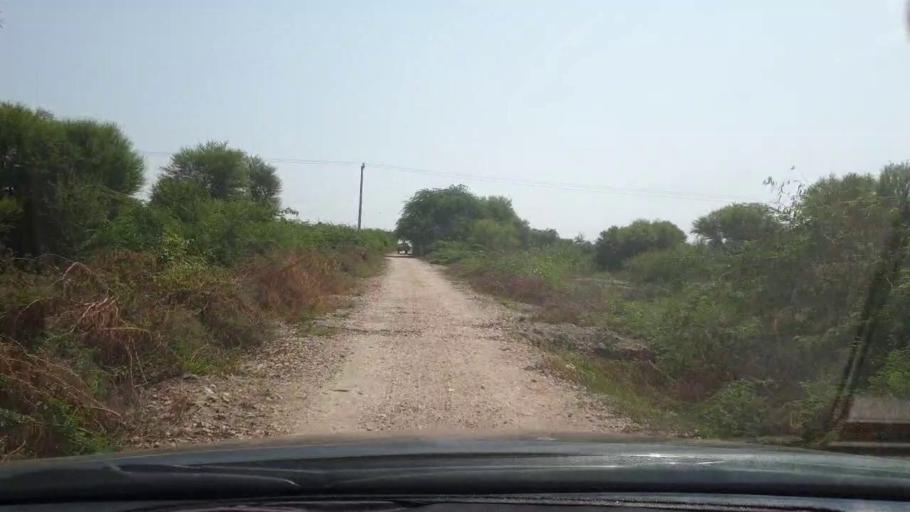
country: PK
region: Sindh
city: Naukot
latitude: 24.8123
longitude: 69.2442
